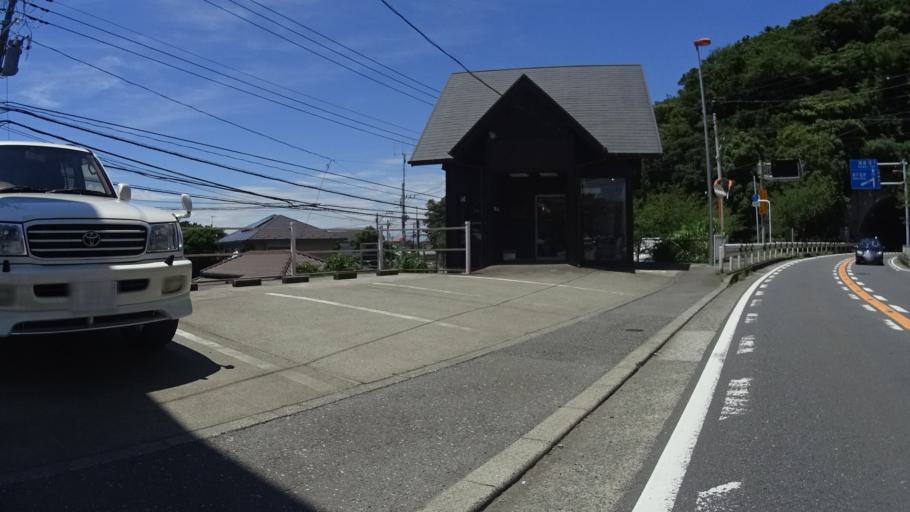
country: JP
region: Kanagawa
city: Hayama
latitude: 35.2736
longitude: 139.5790
